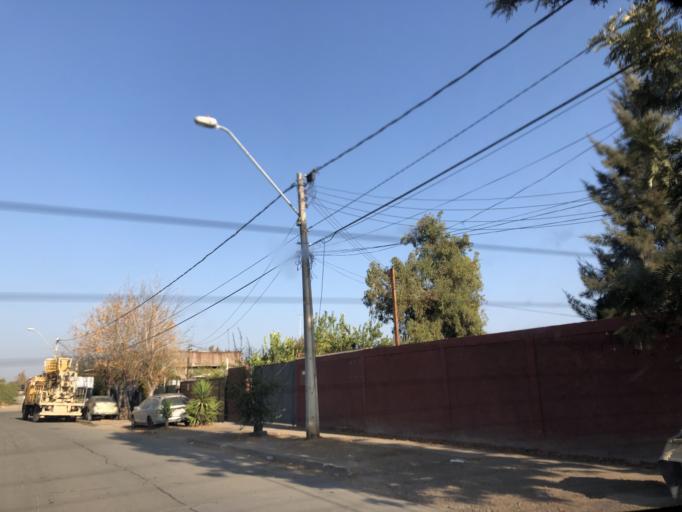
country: CL
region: Santiago Metropolitan
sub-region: Provincia de Cordillera
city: Puente Alto
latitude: -33.6287
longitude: -70.5836
